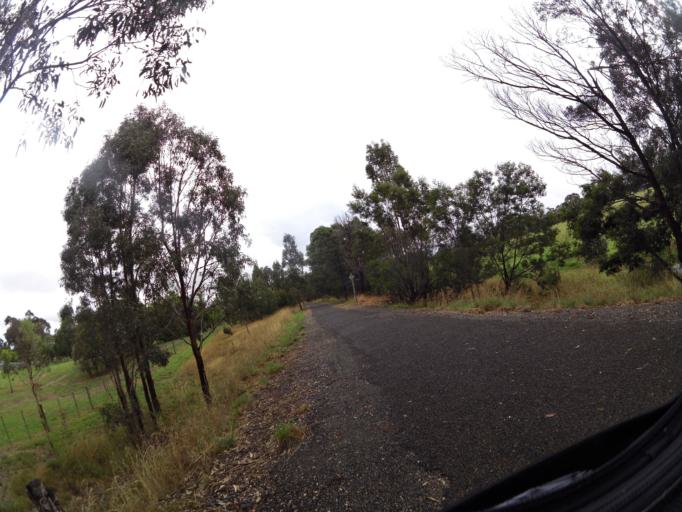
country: AU
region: Victoria
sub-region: East Gippsland
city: Bairnsdale
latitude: -37.8200
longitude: 147.7191
